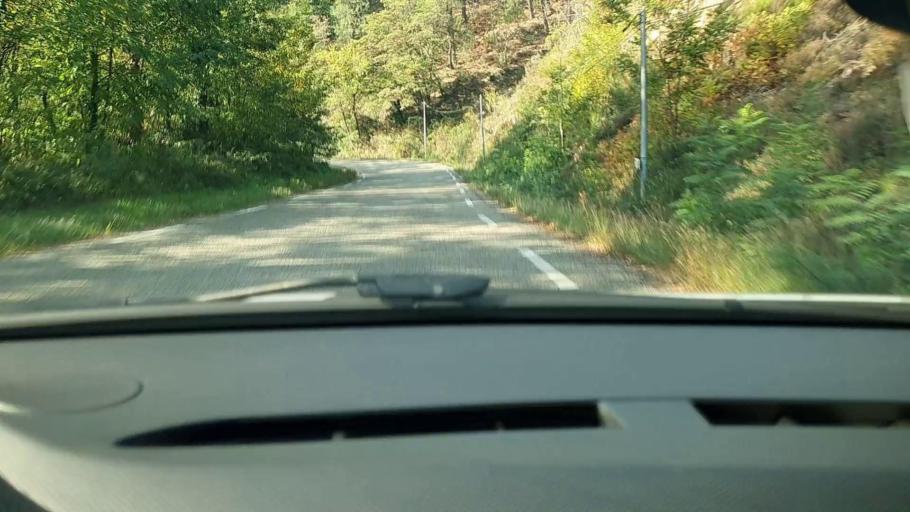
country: FR
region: Languedoc-Roussillon
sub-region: Departement du Gard
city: Besseges
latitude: 44.3108
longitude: 4.0506
